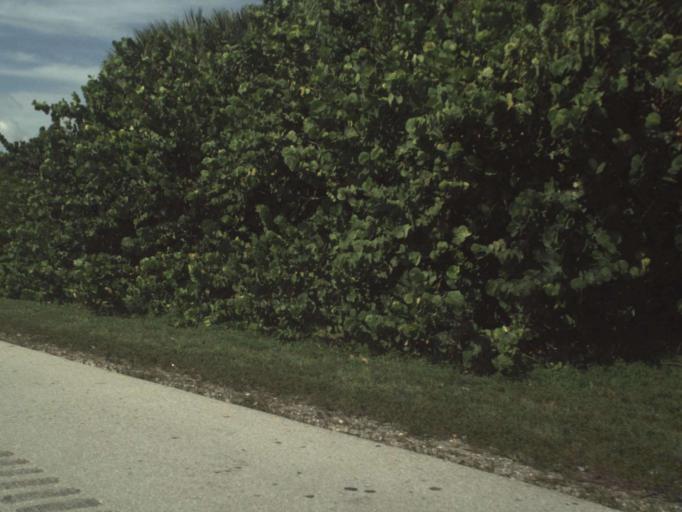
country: US
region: Florida
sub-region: Palm Beach County
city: Mangonia Park
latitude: 26.7443
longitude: -80.0907
